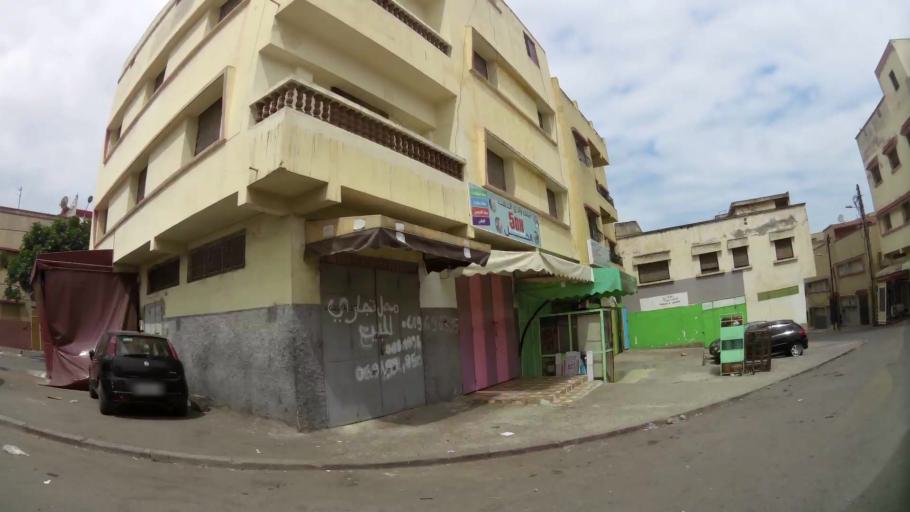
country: MA
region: Rabat-Sale-Zemmour-Zaer
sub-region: Rabat
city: Rabat
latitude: 33.9983
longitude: -6.8712
